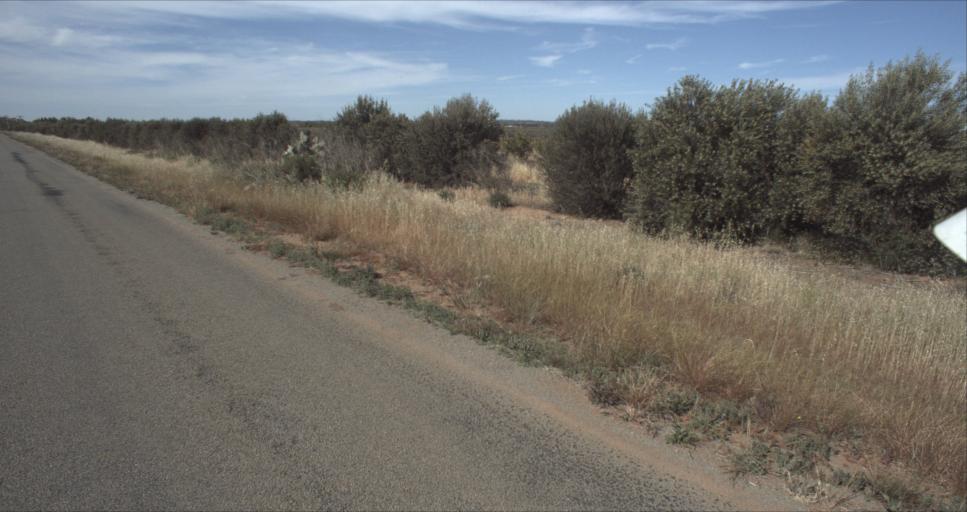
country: AU
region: New South Wales
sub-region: Leeton
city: Leeton
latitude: -34.5690
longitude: 146.4732
